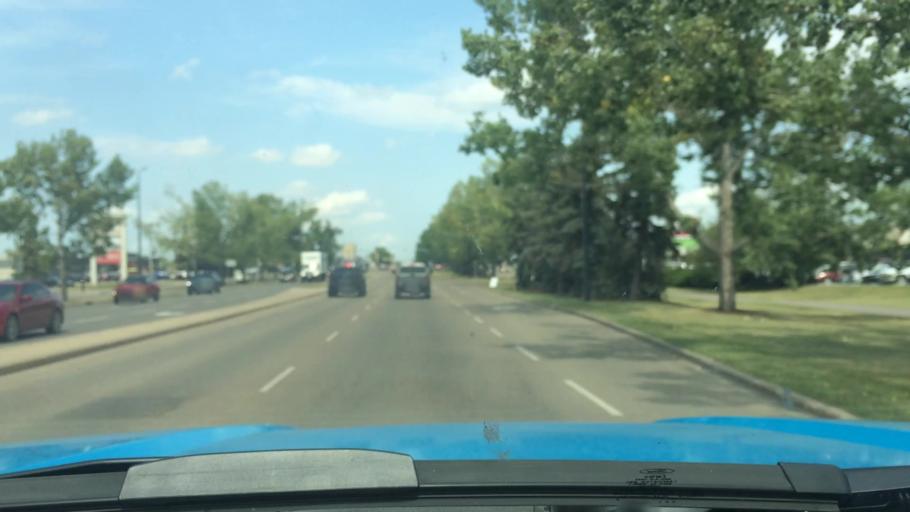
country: CA
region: Alberta
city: Red Deer
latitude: 52.2394
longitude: -113.8139
